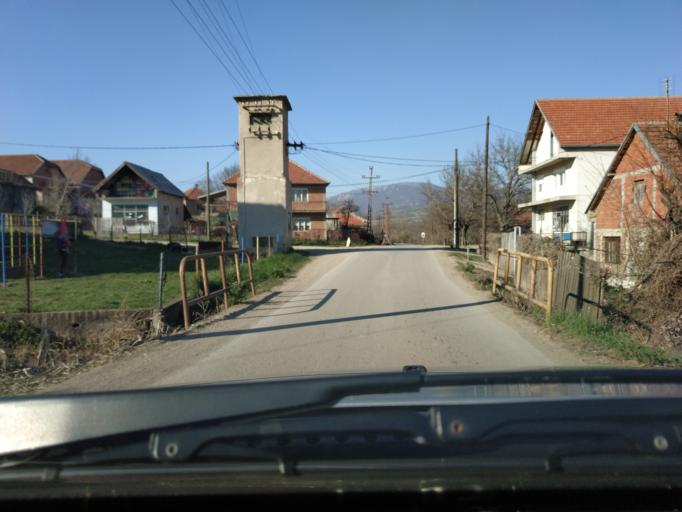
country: RS
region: Central Serbia
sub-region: Nisavski Okrug
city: Aleksinac
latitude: 43.5102
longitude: 21.7978
